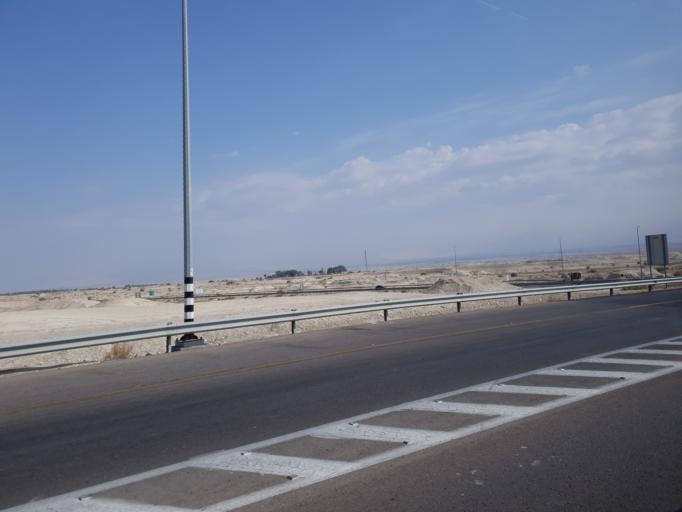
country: PS
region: West Bank
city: Jericho
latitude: 31.7997
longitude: 35.4889
